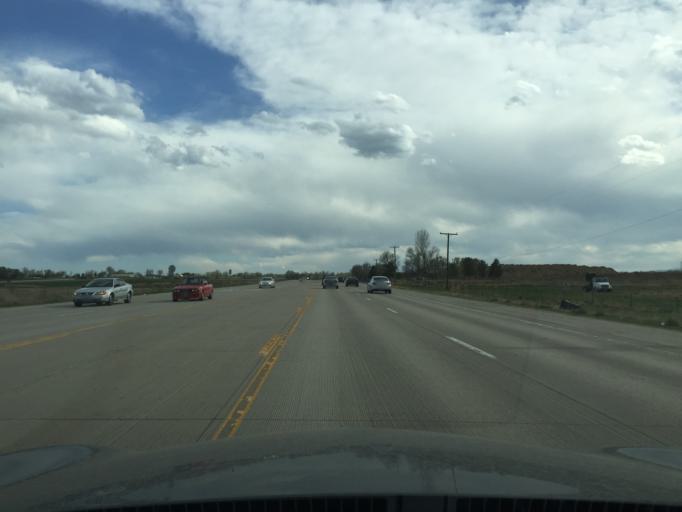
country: US
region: Colorado
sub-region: Boulder County
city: Erie
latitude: 40.0494
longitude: -105.1027
